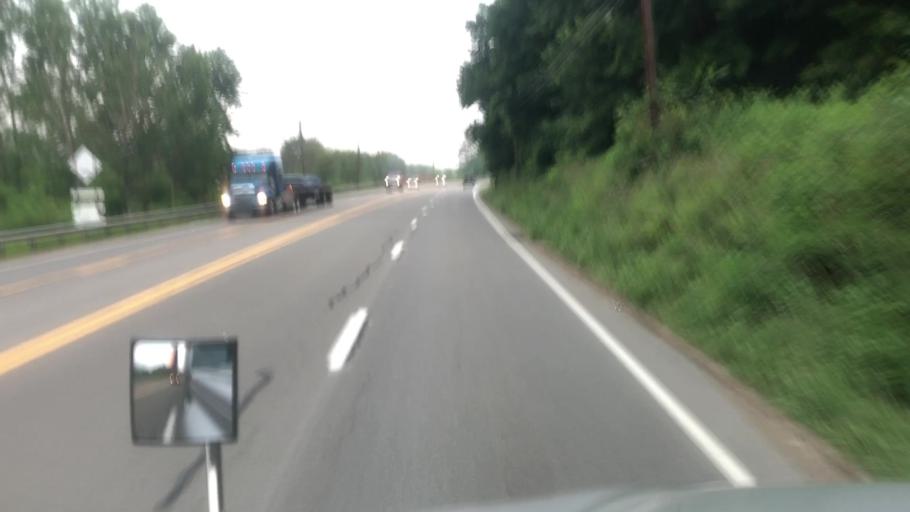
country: US
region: Pennsylvania
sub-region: Venango County
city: Woodland Heights
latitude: 41.4069
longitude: -79.7466
